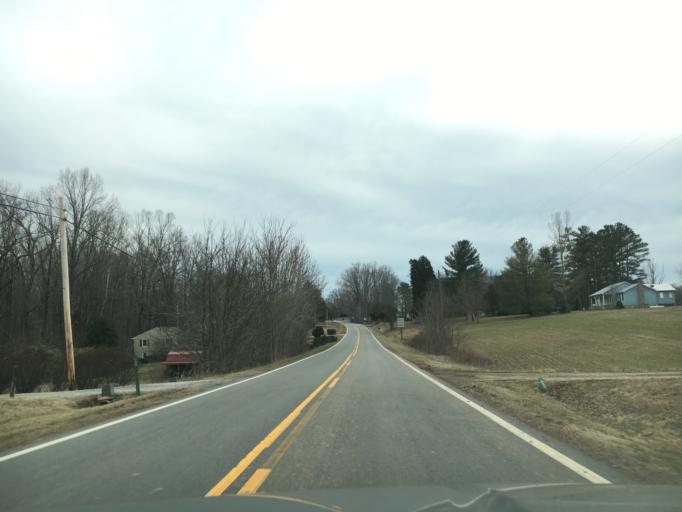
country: US
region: Virginia
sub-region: Charlotte County
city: Charlotte Court House
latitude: 37.0892
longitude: -78.7458
